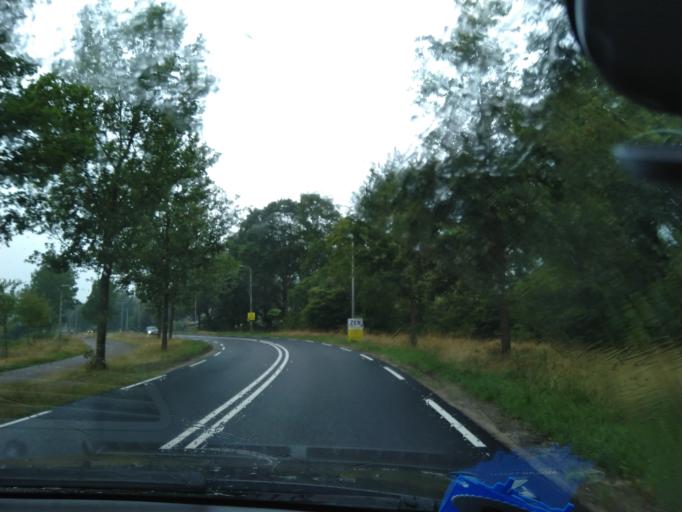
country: NL
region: Overijssel
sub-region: Gemeente Twenterand
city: Den Ham
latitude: 52.3746
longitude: 6.4698
